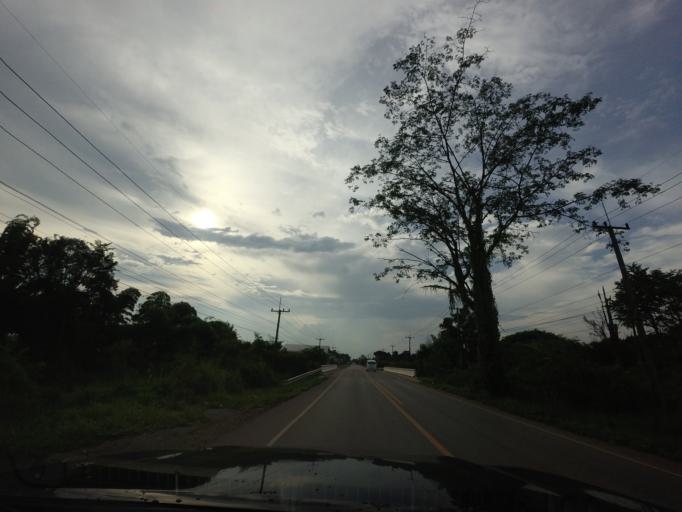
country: TH
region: Changwat Udon Thani
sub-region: Amphoe Ban Phue
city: Ban Phue
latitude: 17.6988
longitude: 102.4471
